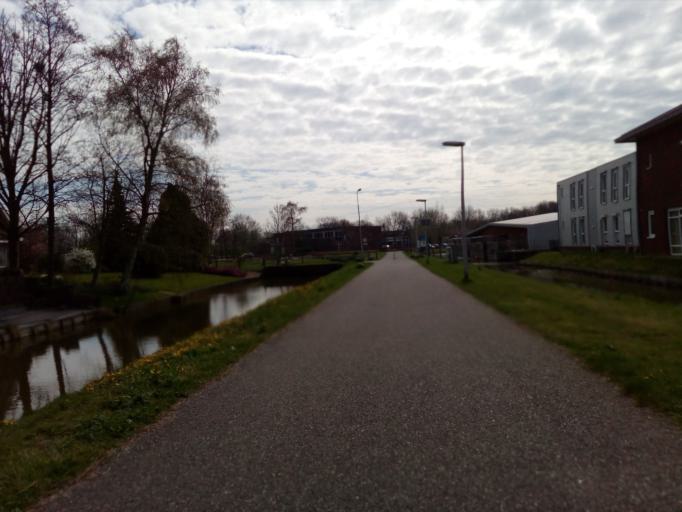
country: NL
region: South Holland
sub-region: Gemeente Den Haag
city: Ypenburg
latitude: 52.0400
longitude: 4.3802
